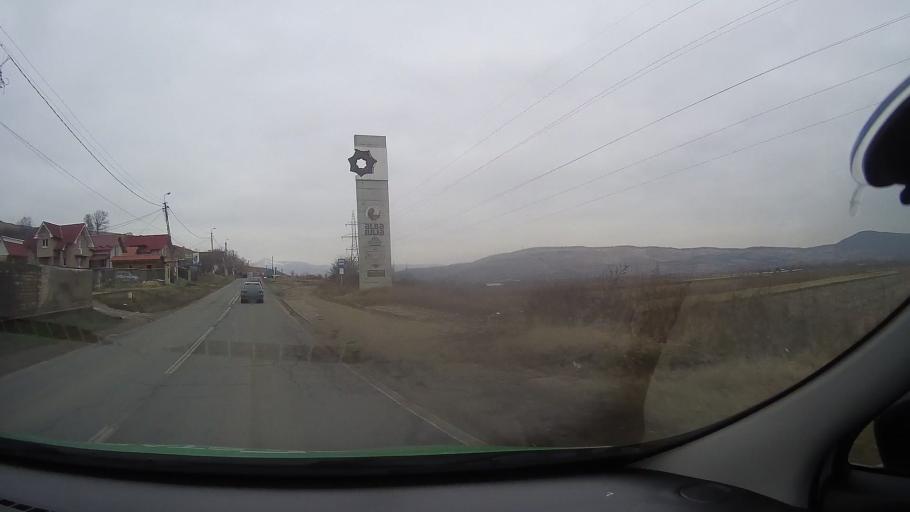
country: RO
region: Alba
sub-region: Comuna Ighiu
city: Sard
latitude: 46.1138
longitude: 23.5387
